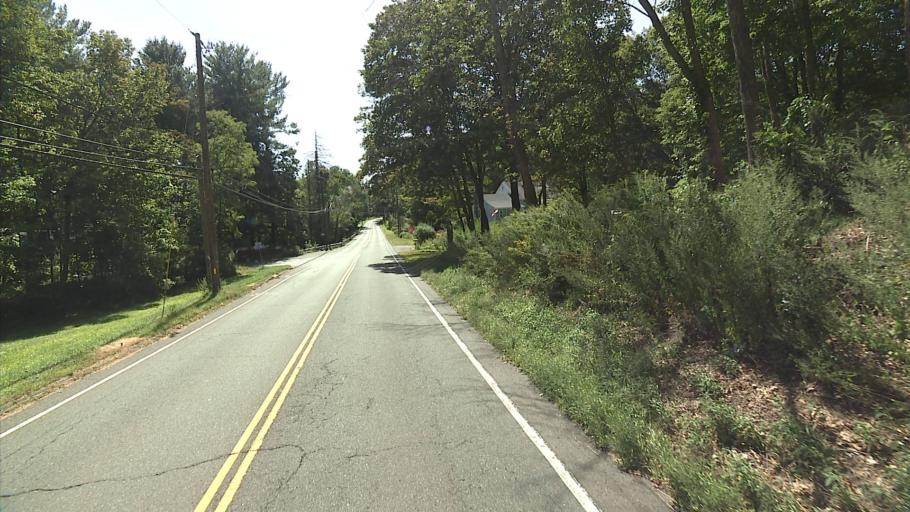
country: US
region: Connecticut
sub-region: New Haven County
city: Southbury
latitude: 41.4766
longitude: -73.1582
